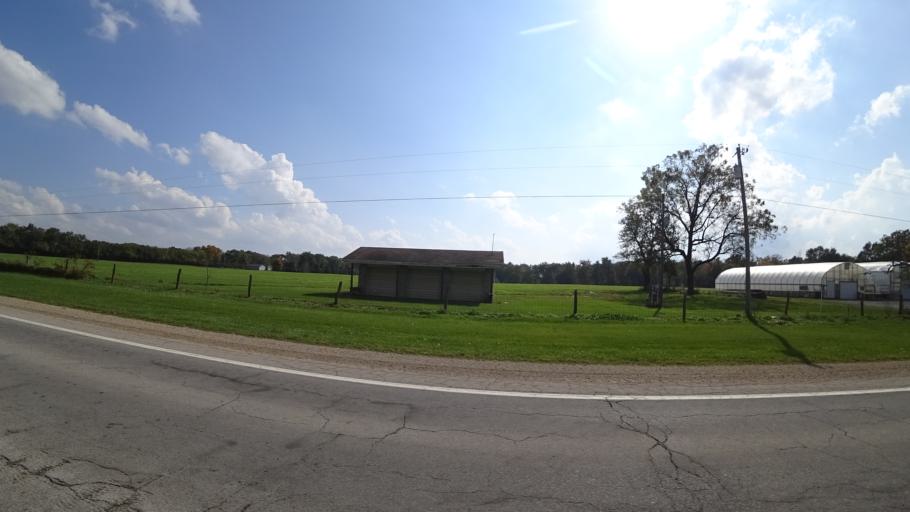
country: US
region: Michigan
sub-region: Saint Joseph County
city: Colon
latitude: 42.0102
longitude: -85.4039
